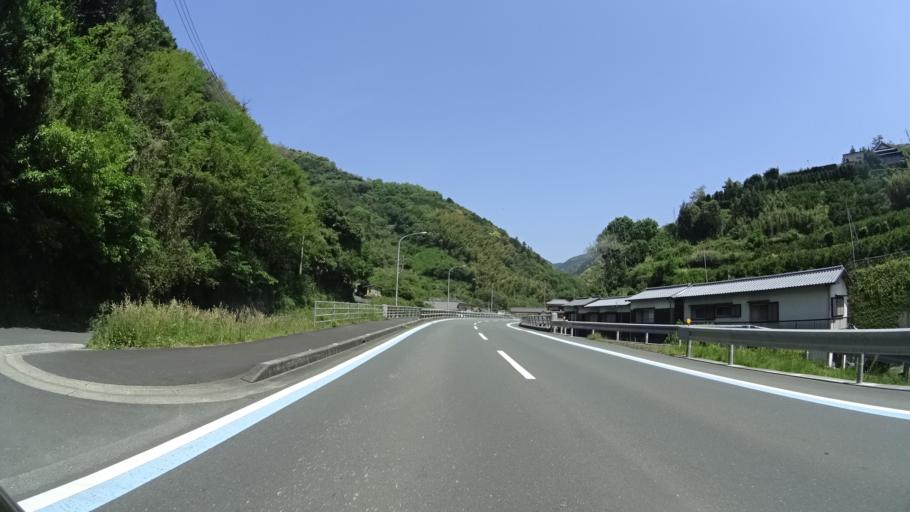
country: JP
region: Ehime
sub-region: Nishiuwa-gun
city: Ikata-cho
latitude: 33.5018
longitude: 132.3963
